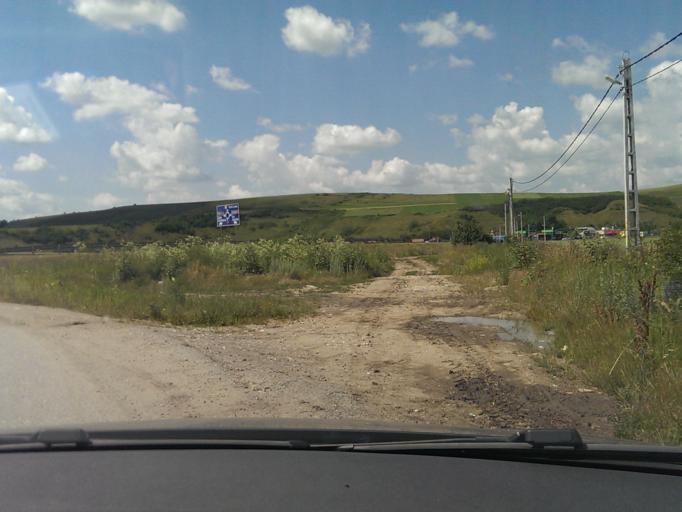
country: RO
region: Cluj
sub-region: Comuna Apahida
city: Sannicoara
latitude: 46.7948
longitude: 23.7185
